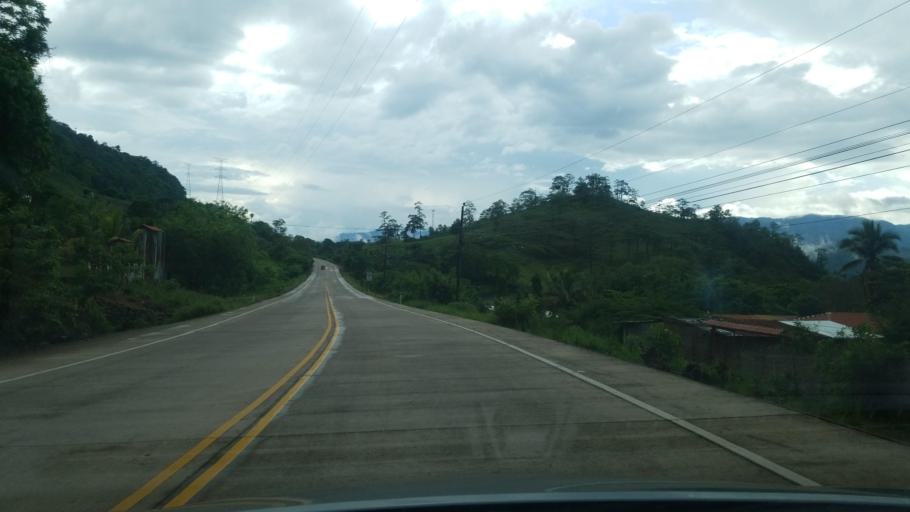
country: HN
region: Copan
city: Copan
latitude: 14.8556
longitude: -89.1999
